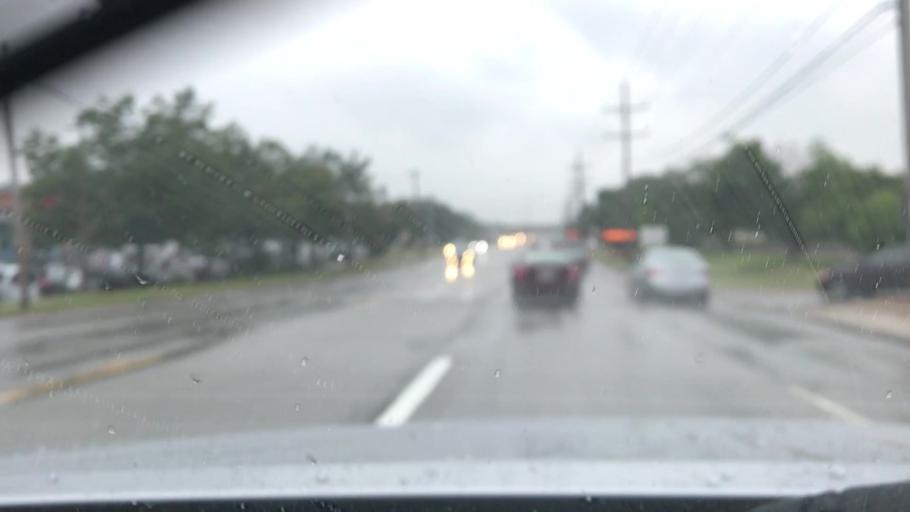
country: US
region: Illinois
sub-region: DuPage County
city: Lisle
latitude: 41.8048
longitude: -88.0482
